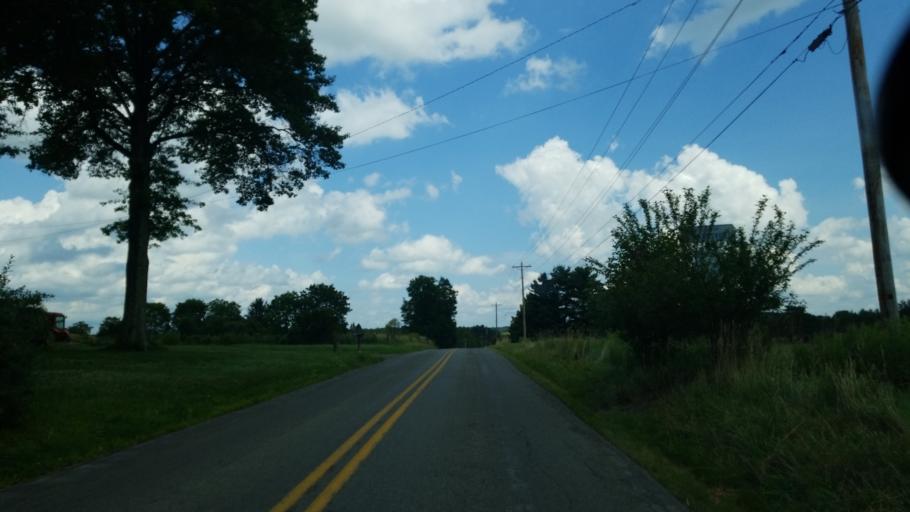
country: US
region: Pennsylvania
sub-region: Jefferson County
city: Brookville
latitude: 41.2392
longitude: -79.0222
